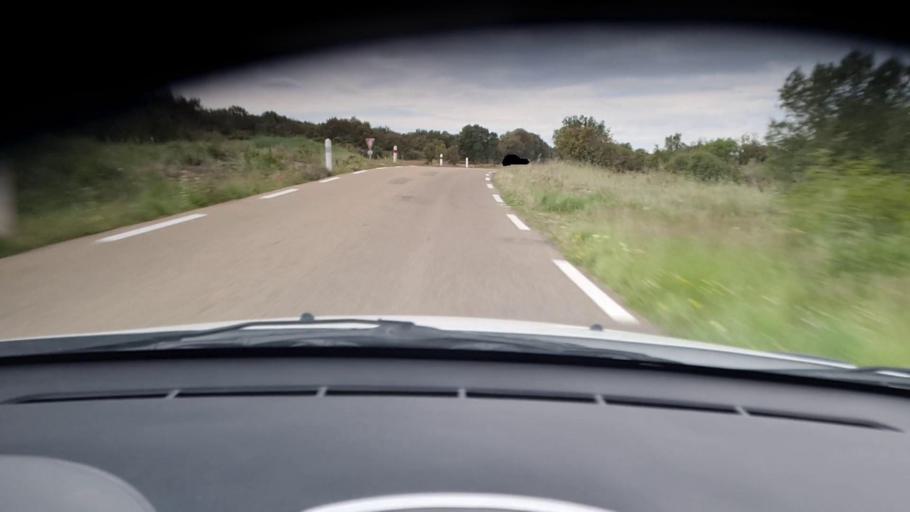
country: FR
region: Languedoc-Roussillon
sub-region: Departement du Gard
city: Blauzac
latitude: 43.9772
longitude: 4.4039
